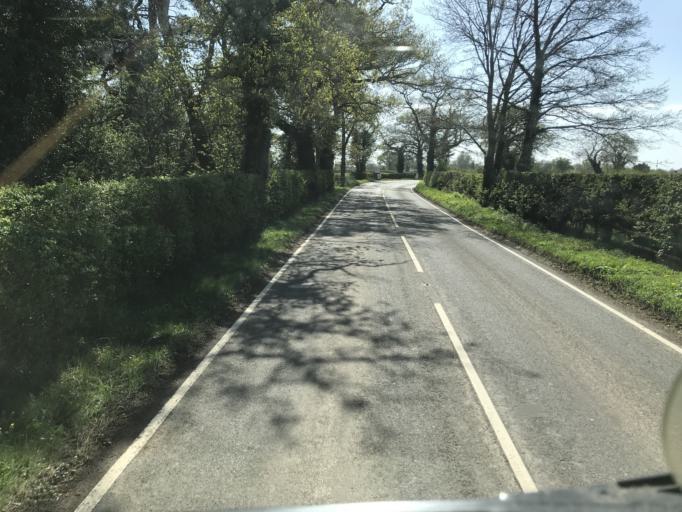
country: GB
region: England
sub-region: Cheshire East
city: Nantwich
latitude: 53.0941
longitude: -2.5146
